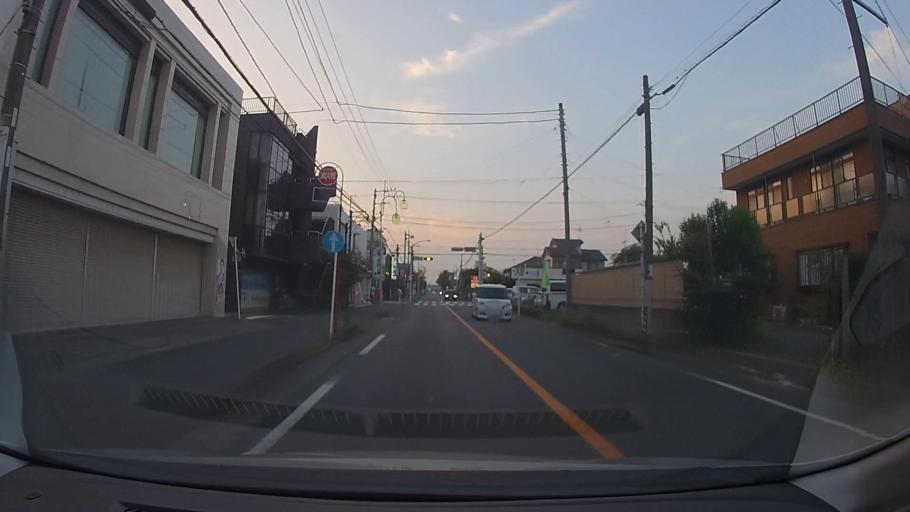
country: JP
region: Kanagawa
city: Minami-rinkan
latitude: 35.4756
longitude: 139.4549
